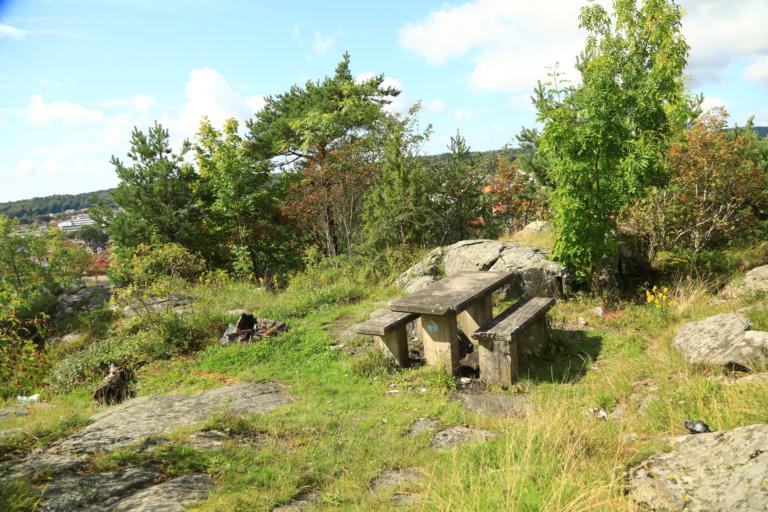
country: SE
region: Halland
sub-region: Kungsbacka Kommun
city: Kungsbacka
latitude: 57.4953
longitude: 12.0838
